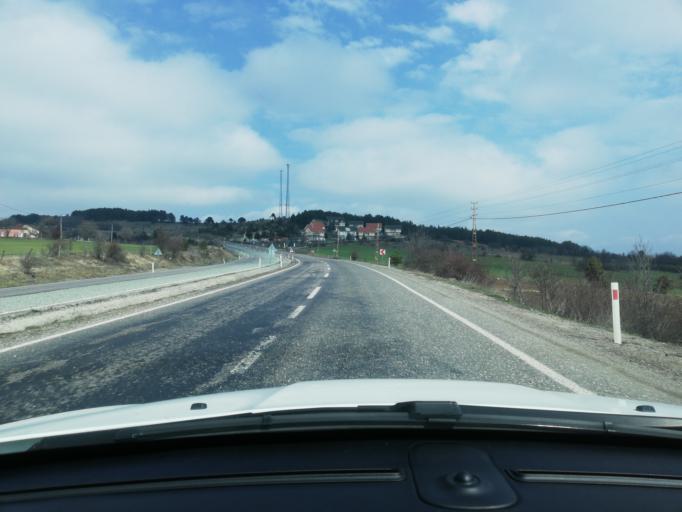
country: TR
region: Kastamonu
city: Kuzyaka
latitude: 41.2325
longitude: 33.7937
